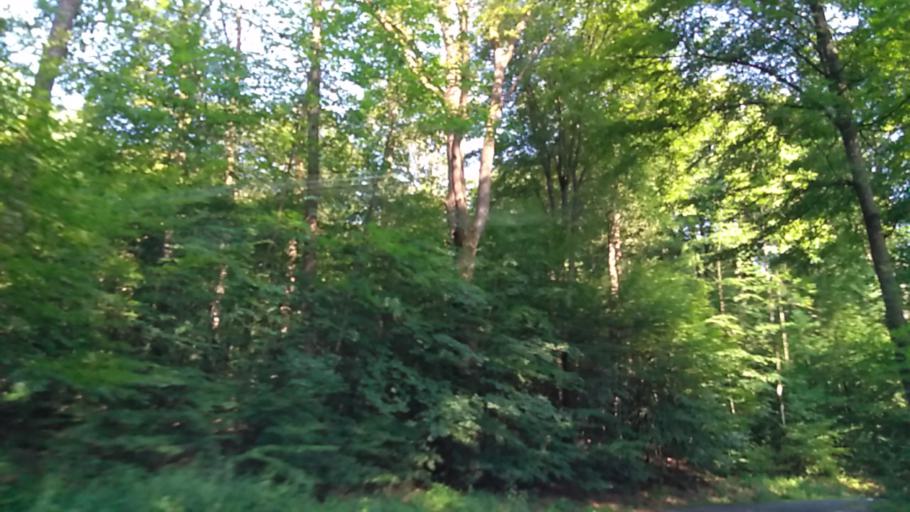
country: DE
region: North Rhine-Westphalia
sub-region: Regierungsbezirk Arnsberg
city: Luedenscheid
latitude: 51.2055
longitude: 7.6769
